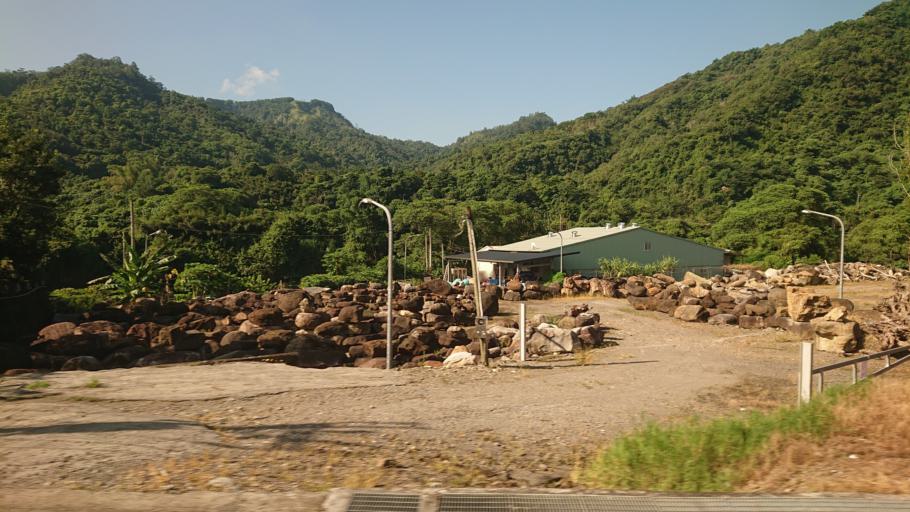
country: TW
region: Taiwan
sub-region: Nantou
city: Puli
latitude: 24.0583
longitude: 120.9040
